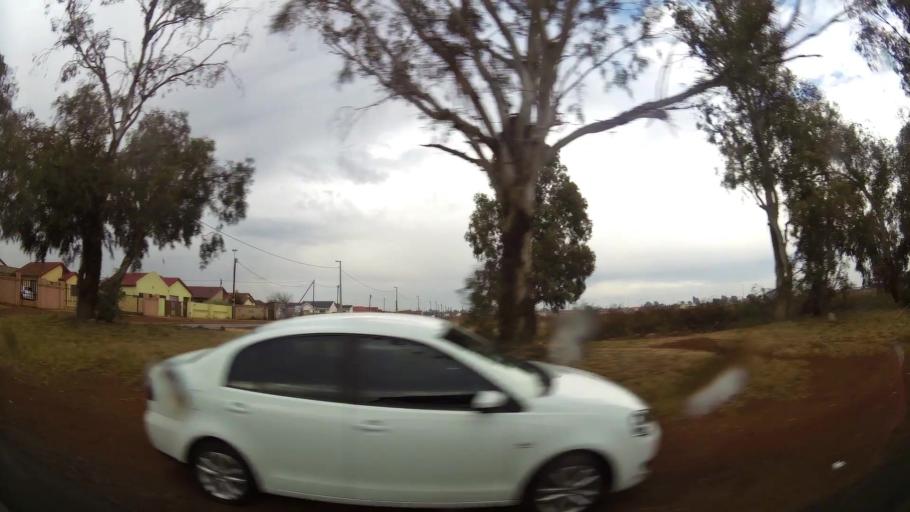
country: ZA
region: Gauteng
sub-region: Ekurhuleni Metropolitan Municipality
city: Germiston
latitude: -26.3284
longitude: 28.1995
